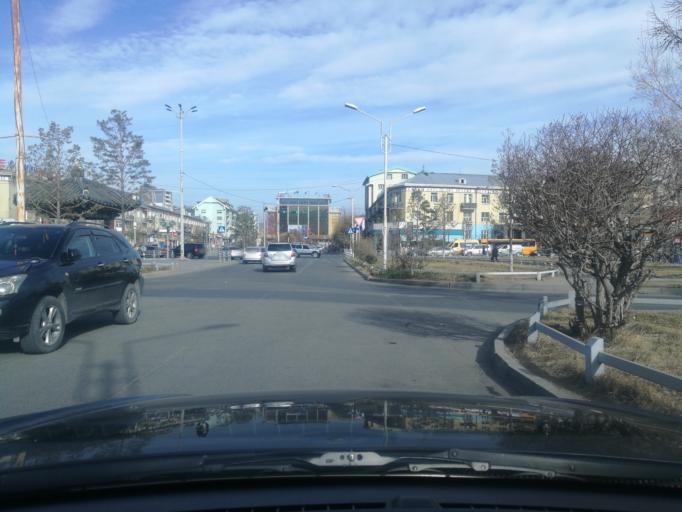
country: MN
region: Ulaanbaatar
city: Ulaanbaatar
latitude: 47.9130
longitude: 106.9073
